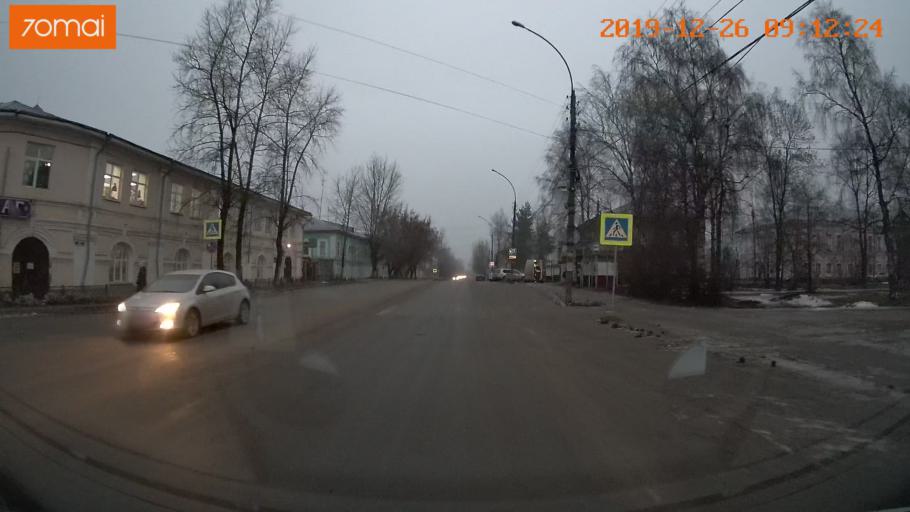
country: RU
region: Vologda
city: Gryazovets
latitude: 58.8808
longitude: 40.2534
